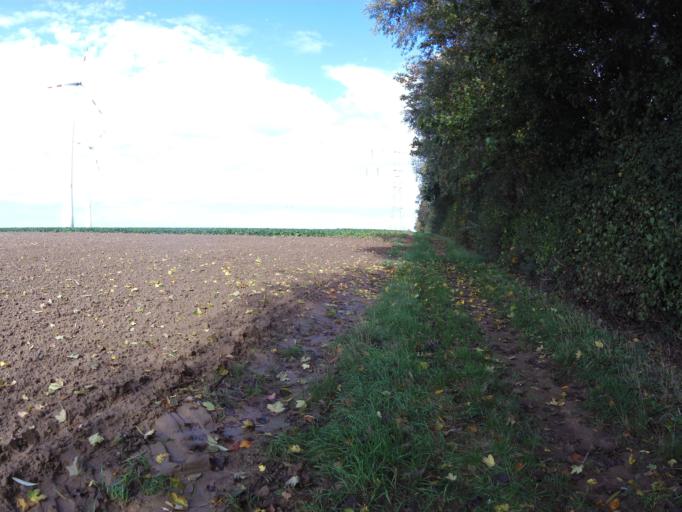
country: DE
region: Bavaria
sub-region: Regierungsbezirk Unterfranken
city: Sommerhausen
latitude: 49.7143
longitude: 10.0578
